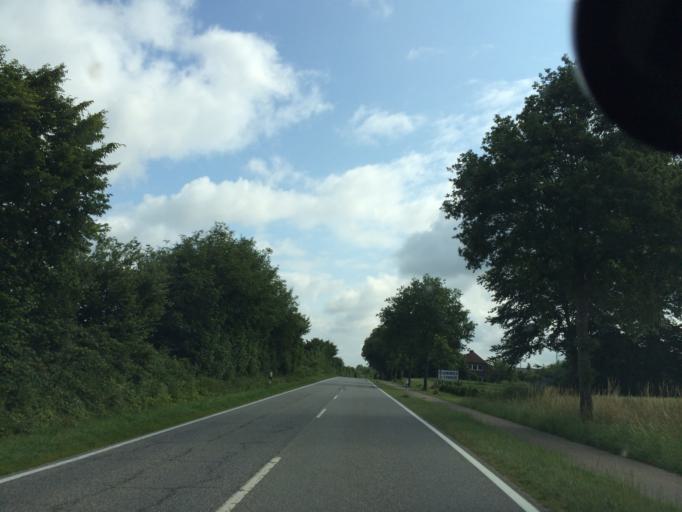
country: DE
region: Schleswig-Holstein
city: Holtsee
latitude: 54.3975
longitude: 9.8640
